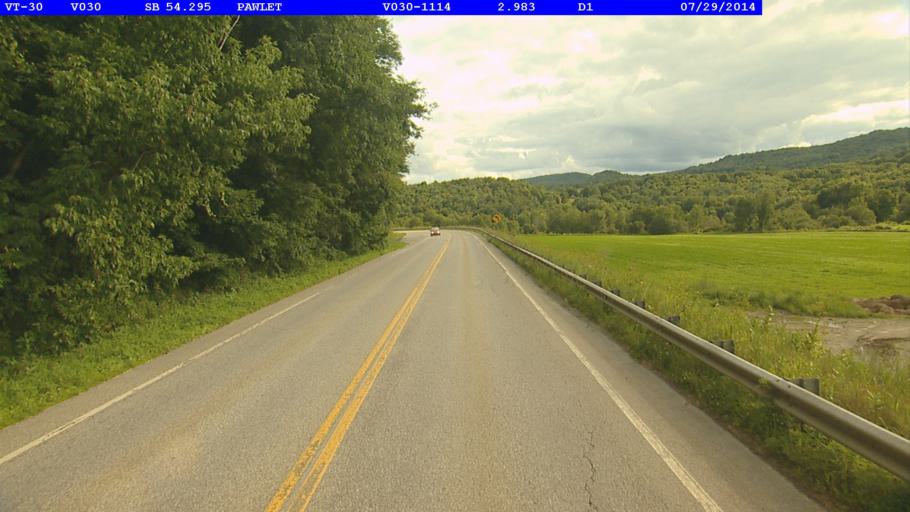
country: US
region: New York
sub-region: Washington County
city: Granville
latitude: 43.3505
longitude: -73.1822
